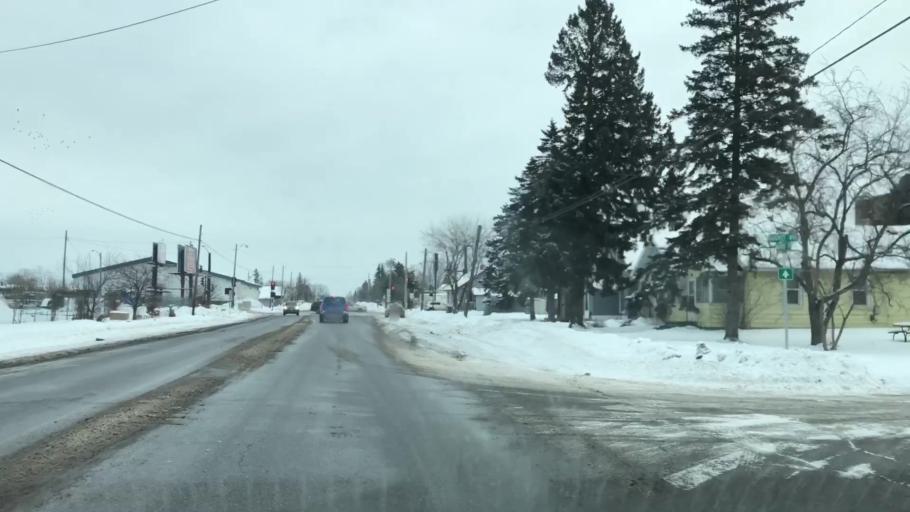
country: US
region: Wisconsin
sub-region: Douglas County
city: Superior
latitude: 46.7279
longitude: -92.0994
